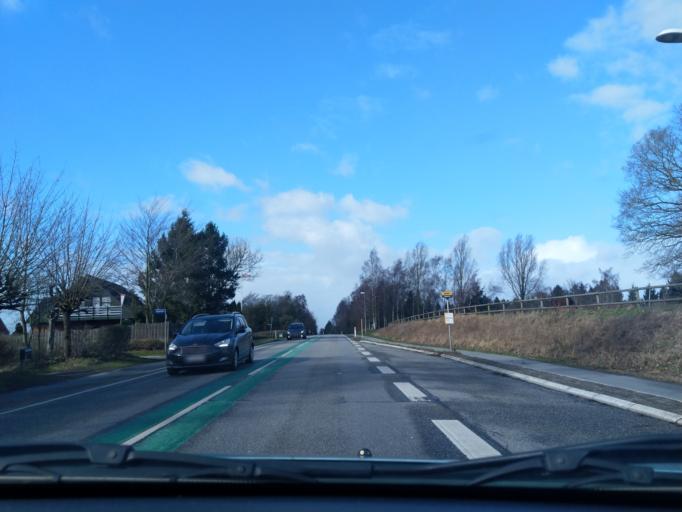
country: DK
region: Zealand
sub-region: Naestved Kommune
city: Naestved
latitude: 55.2669
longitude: 11.7451
